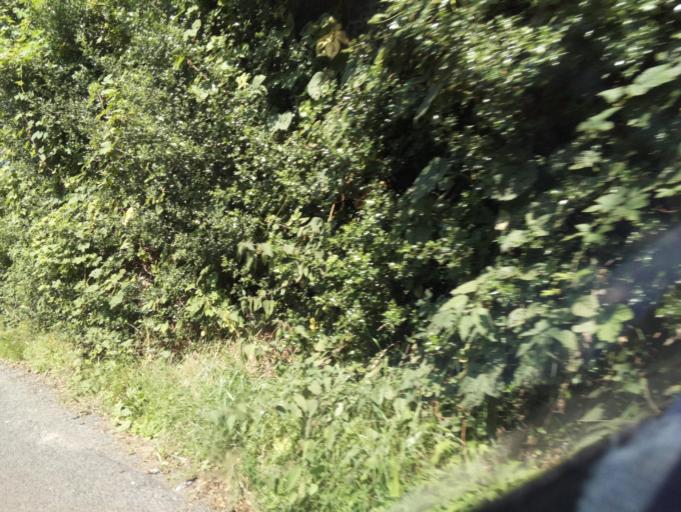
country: GB
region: England
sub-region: Hampshire
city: Kingsclere
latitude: 51.3437
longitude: -1.2805
